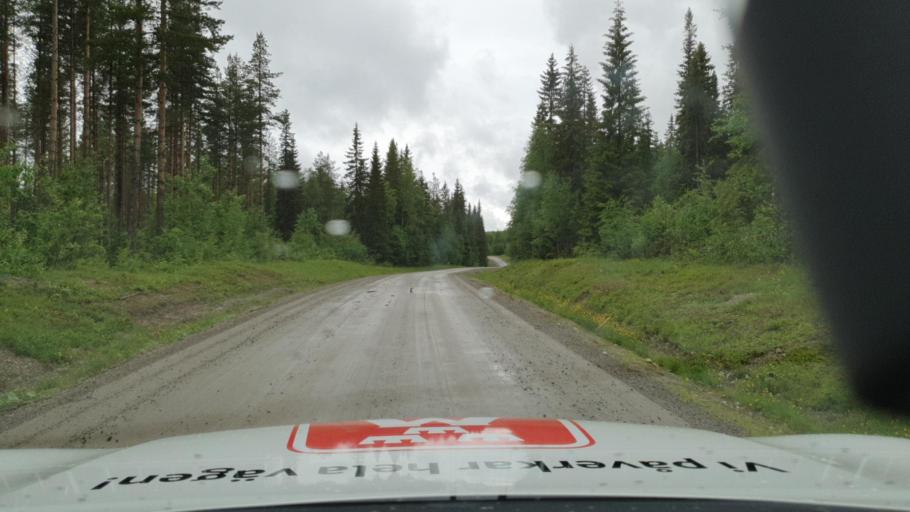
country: SE
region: Vaesterbotten
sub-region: Dorotea Kommun
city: Dorotea
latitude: 64.0551
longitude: 16.7239
